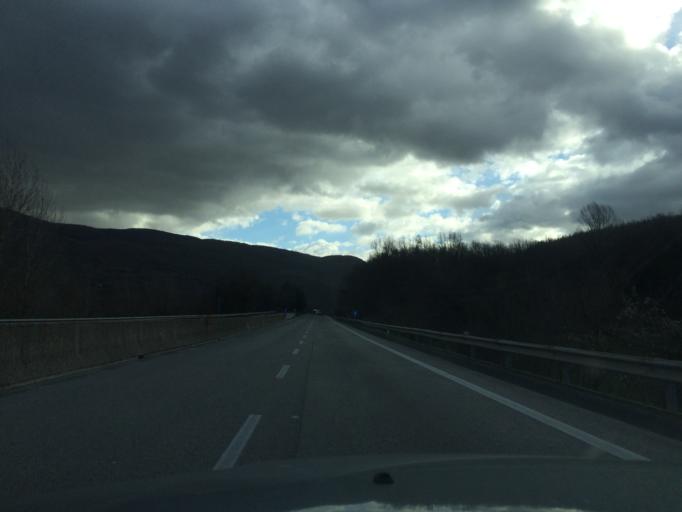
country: IT
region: Umbria
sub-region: Provincia di Terni
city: Acquasparta
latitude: 42.7225
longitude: 12.5431
